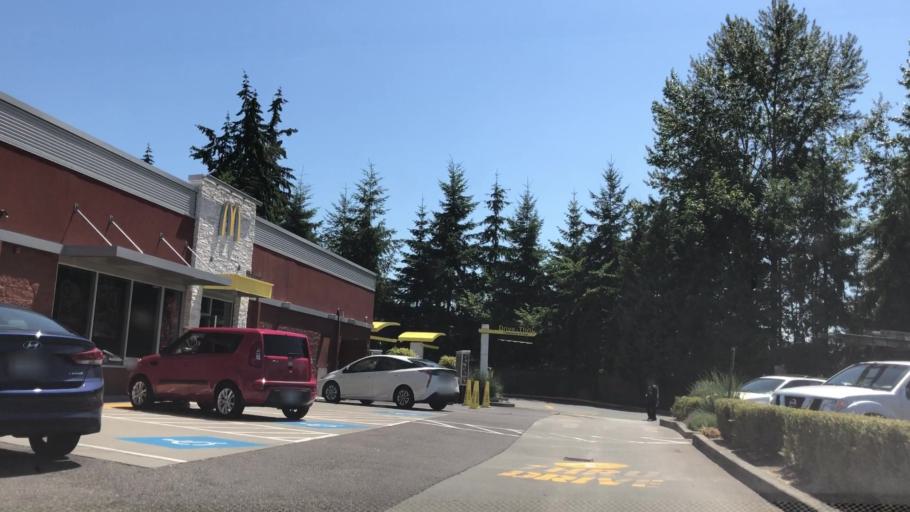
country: US
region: Washington
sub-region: Snohomish County
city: Alderwood Manor
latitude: 47.8206
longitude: -122.2688
